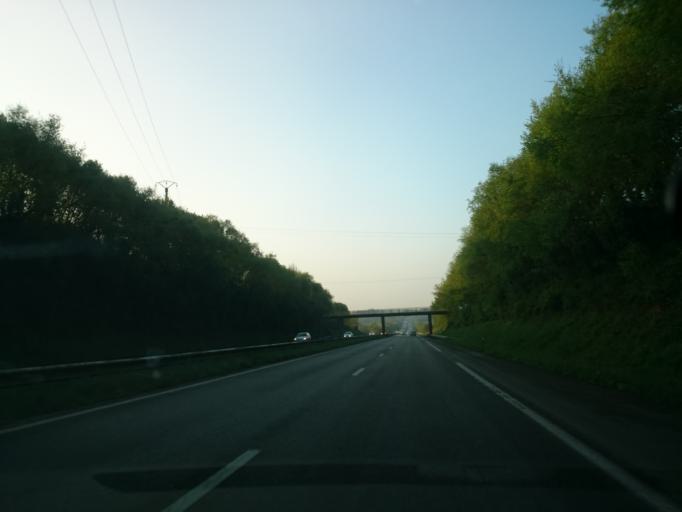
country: FR
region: Brittany
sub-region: Departement du Finistere
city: Briec
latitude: 48.1437
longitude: -4.0317
